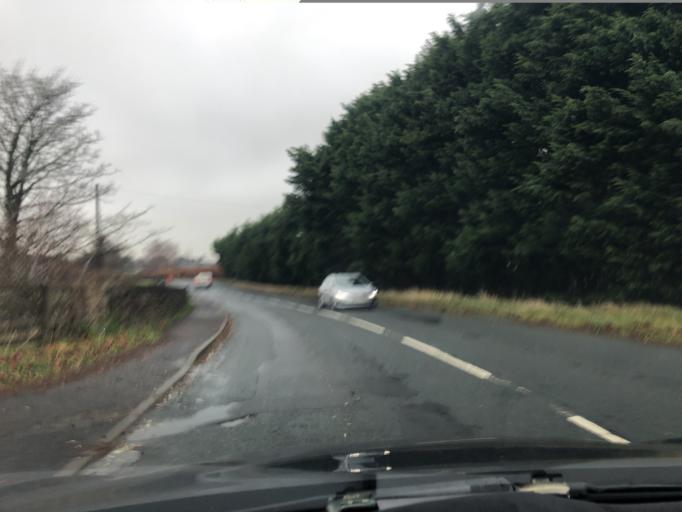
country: GB
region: England
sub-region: North Yorkshire
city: Stokesley
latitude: 54.4633
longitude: -1.1816
